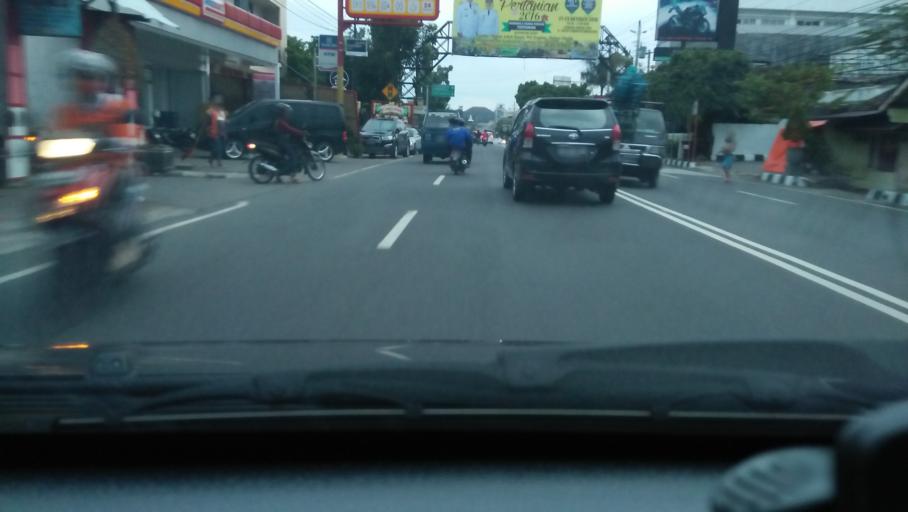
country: ID
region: Central Java
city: Magelang
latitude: -7.4521
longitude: 110.2238
